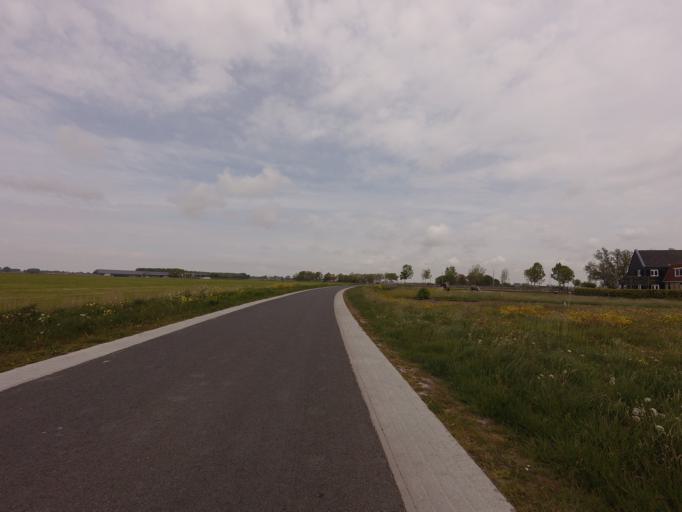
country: NL
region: Friesland
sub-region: Sudwest Fryslan
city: Bolsward
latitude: 53.0850
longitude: 5.4826
